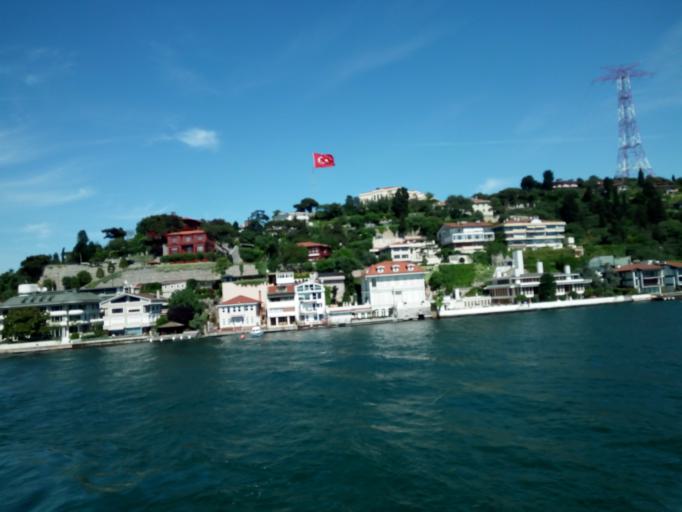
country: TR
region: Istanbul
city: UEskuedar
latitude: 41.0725
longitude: 29.0537
